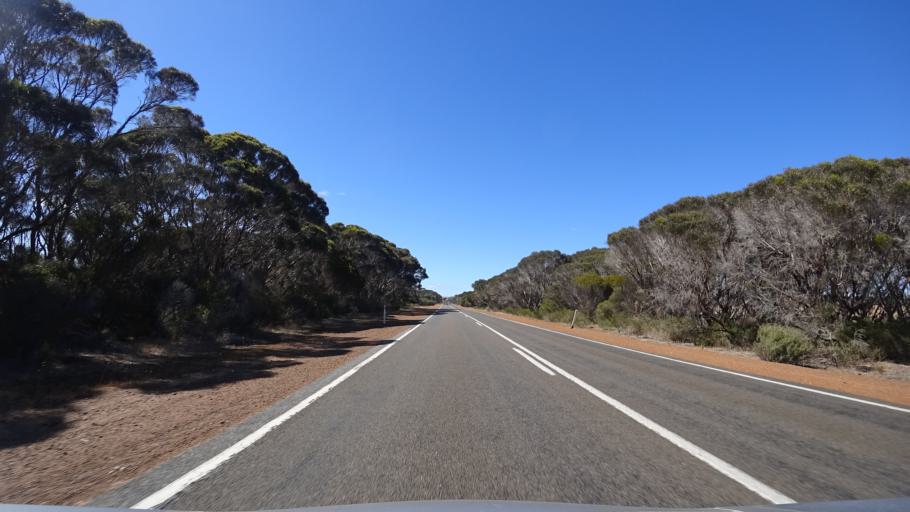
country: AU
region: South Australia
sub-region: Kangaroo Island
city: Kingscote
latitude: -35.7185
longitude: 137.5596
